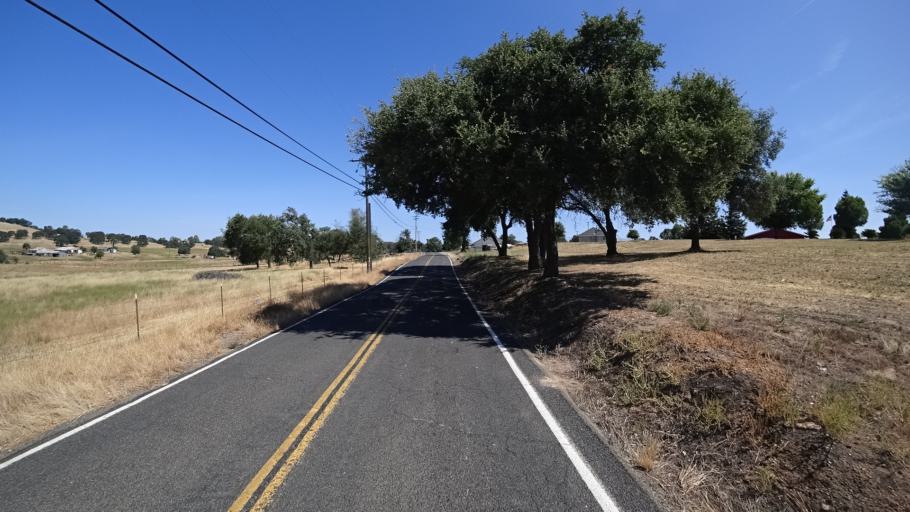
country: US
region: California
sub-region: Calaveras County
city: Rancho Calaveras
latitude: 38.1550
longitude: -120.8949
